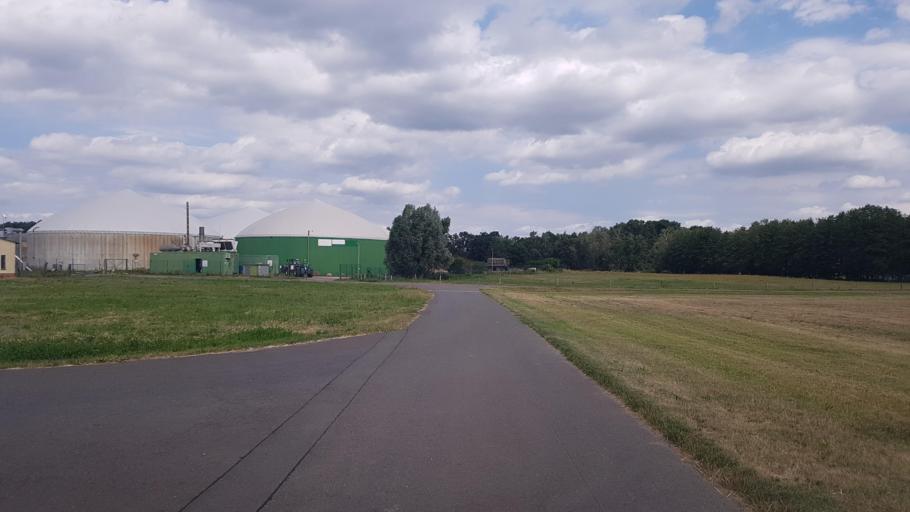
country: DE
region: Brandenburg
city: Juterbog
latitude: 51.9648
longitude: 13.0529
